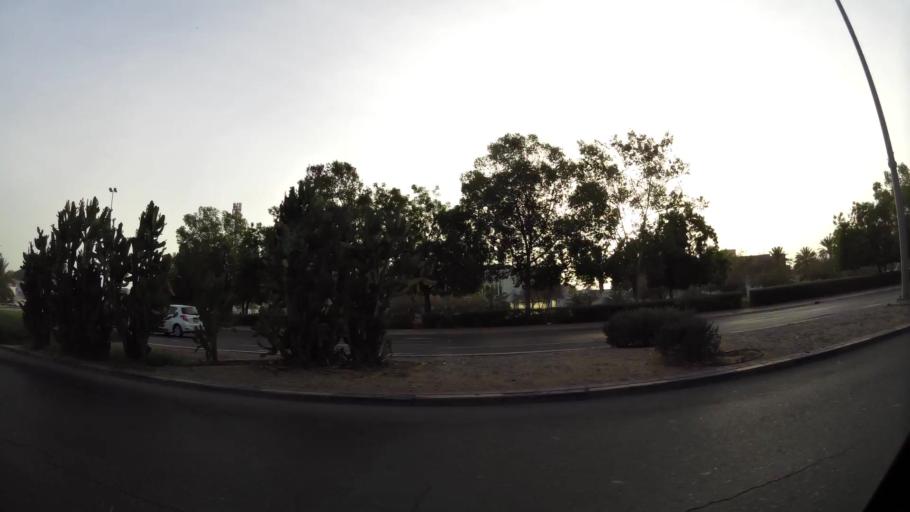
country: AE
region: Abu Dhabi
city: Al Ain
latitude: 24.2491
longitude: 55.7197
